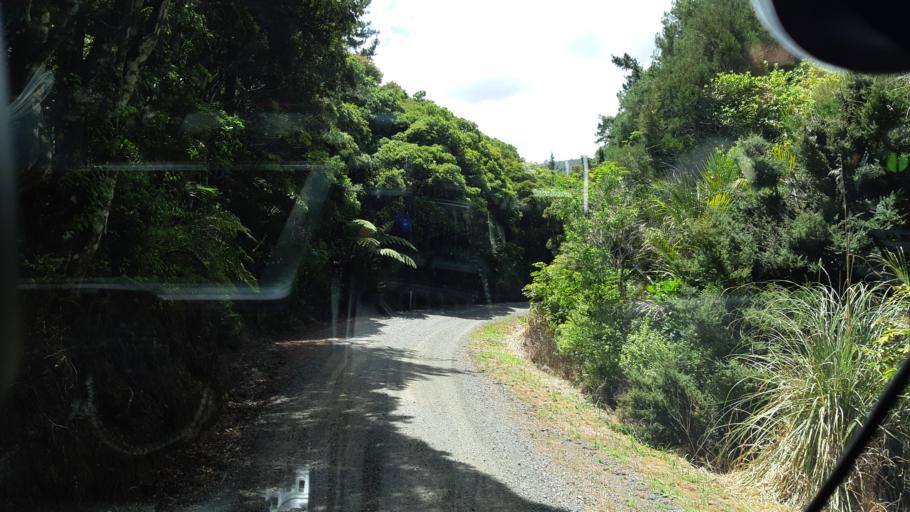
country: NZ
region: Northland
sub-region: Far North District
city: Kaitaia
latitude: -35.2262
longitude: 173.3117
